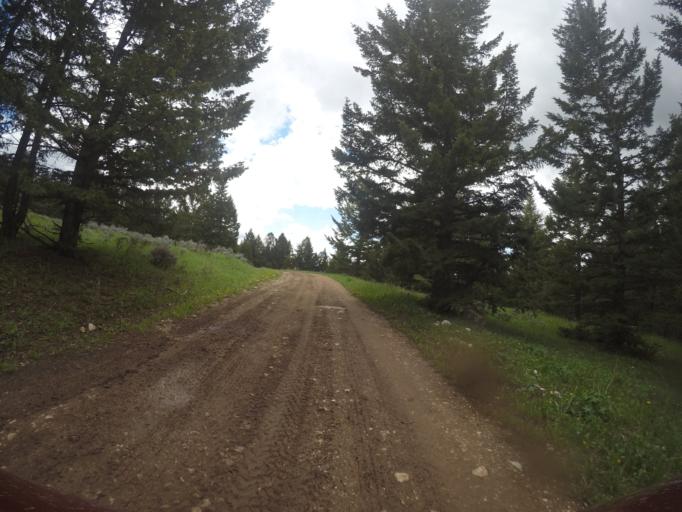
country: US
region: Wyoming
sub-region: Big Horn County
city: Lovell
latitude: 45.1723
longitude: -108.4338
